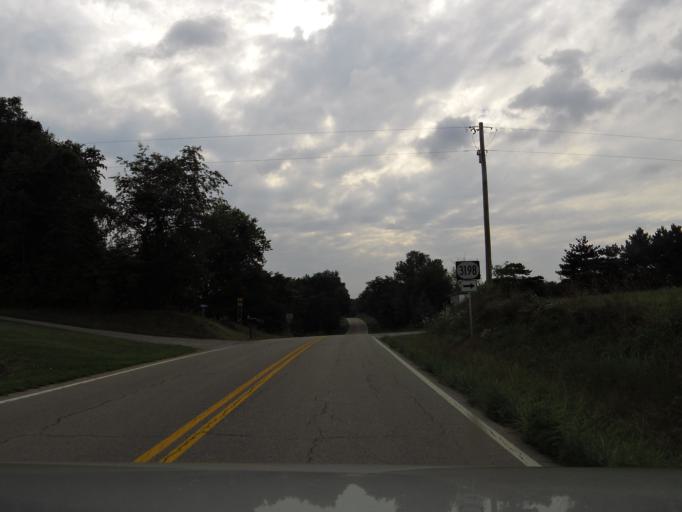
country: US
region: Kentucky
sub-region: Robertson County
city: Mount Olivet
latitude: 38.4931
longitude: -84.1213
